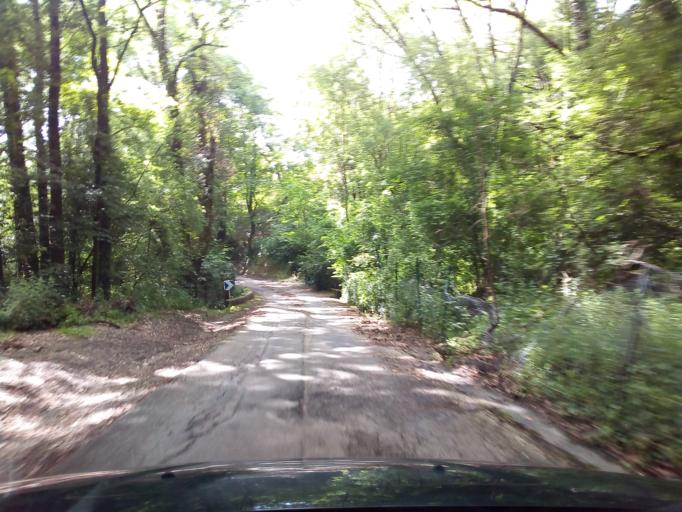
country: FR
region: Rhone-Alpes
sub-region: Departement de l'Isere
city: Saint-Martin-d'Heres
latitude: 45.1681
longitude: 5.7750
